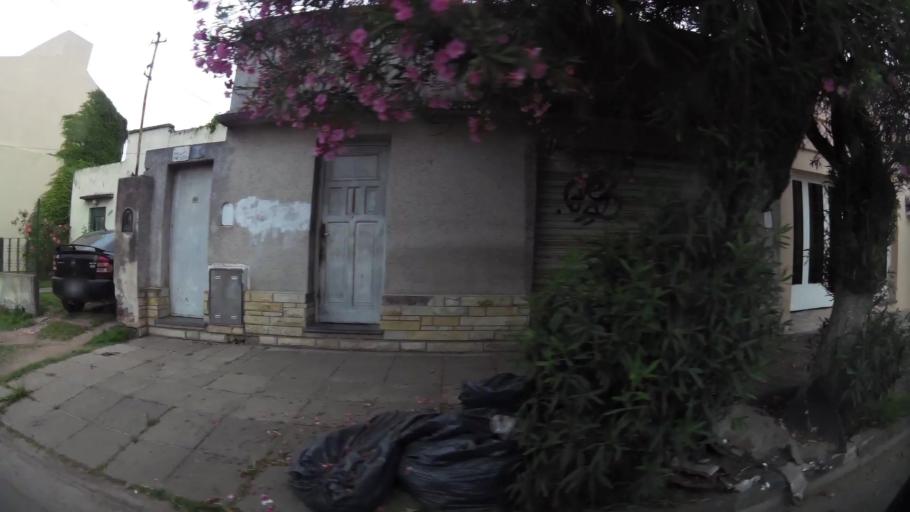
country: AR
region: Buenos Aires
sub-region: Partido de Zarate
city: Zarate
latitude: -34.0955
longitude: -59.0310
